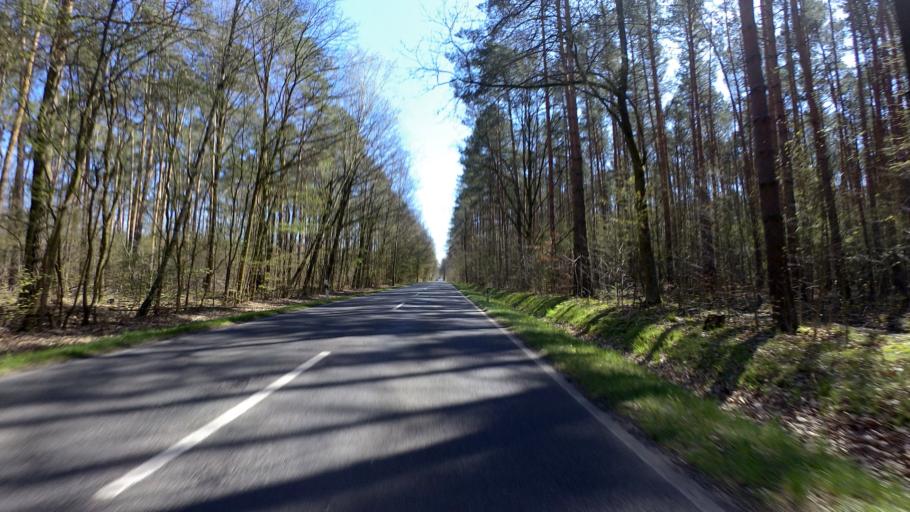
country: DE
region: Brandenburg
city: Schulzendorf
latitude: 52.3397
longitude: 13.5828
